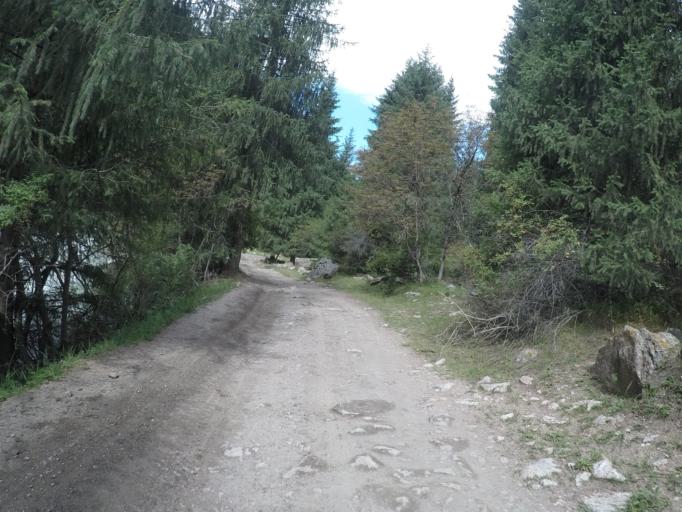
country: KG
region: Ysyk-Koel
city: Teploklyuchenka
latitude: 42.4427
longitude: 78.5533
